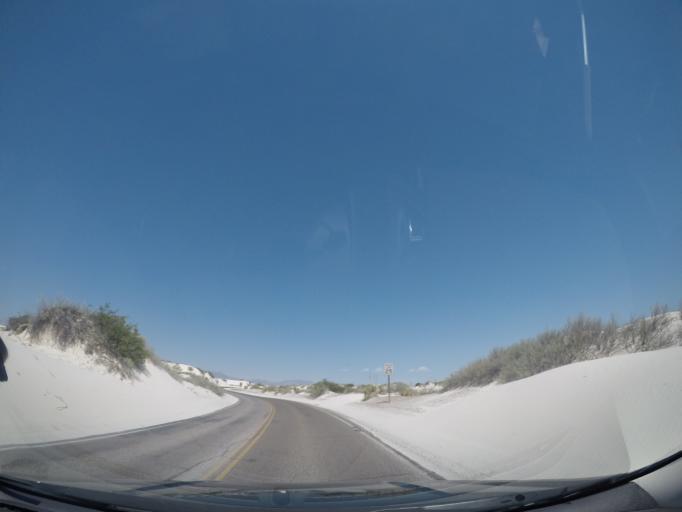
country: US
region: New Mexico
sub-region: Otero County
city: Holloman Air Force Base
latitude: 32.7931
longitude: -106.2373
